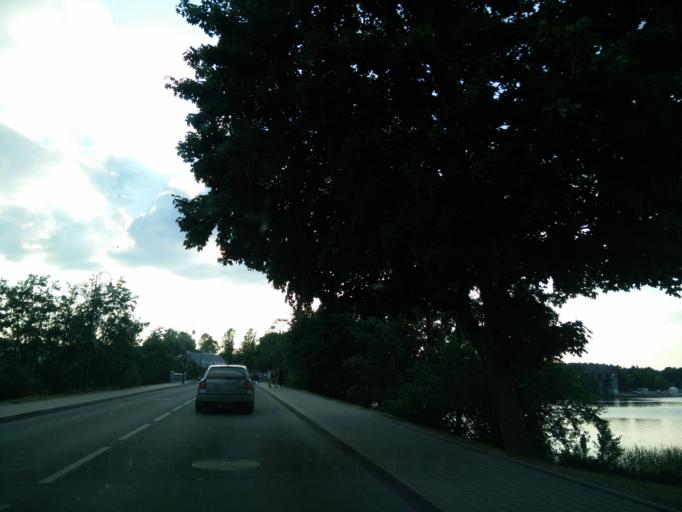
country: LT
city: Trakai
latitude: 54.6498
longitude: 24.9282
